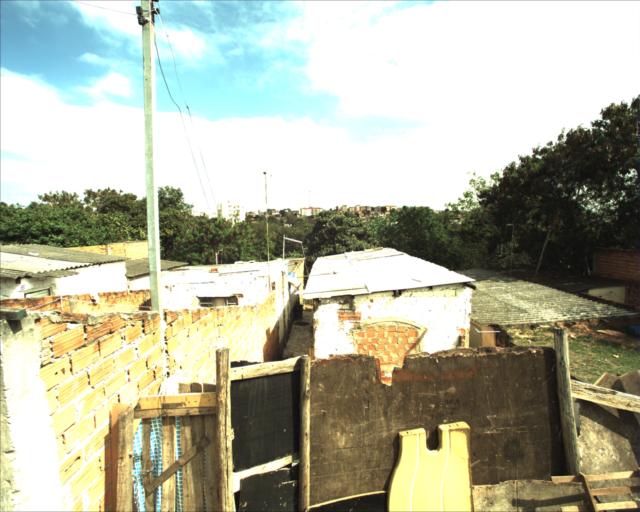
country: BR
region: Sao Paulo
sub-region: Sorocaba
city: Sorocaba
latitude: -23.4983
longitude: -47.4907
